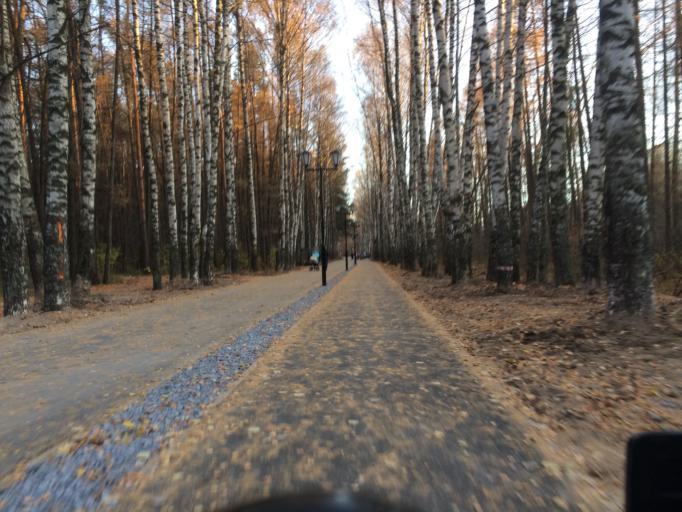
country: RU
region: Mariy-El
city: Yoshkar-Ola
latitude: 56.6257
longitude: 47.9164
